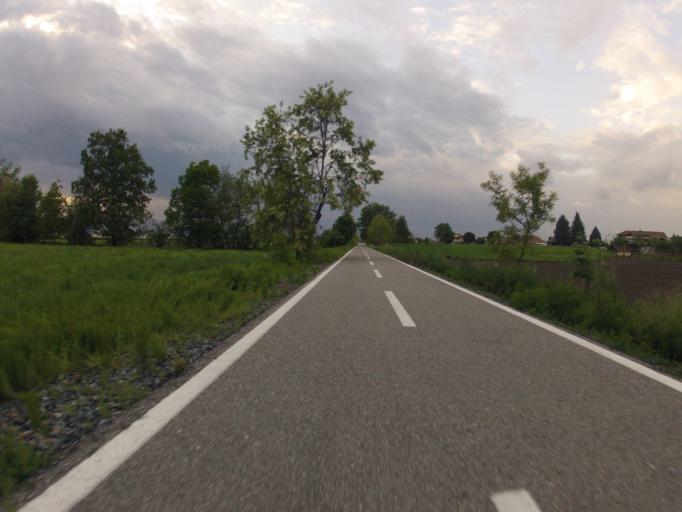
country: IT
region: Piedmont
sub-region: Provincia di Torino
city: Vigone
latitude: 44.8327
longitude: 7.4927
